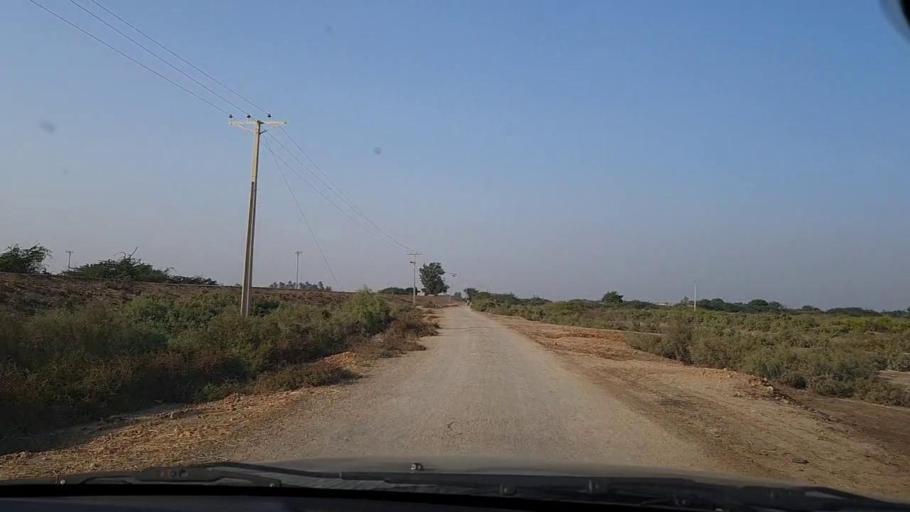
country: PK
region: Sindh
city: Chuhar Jamali
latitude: 24.2926
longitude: 67.7551
